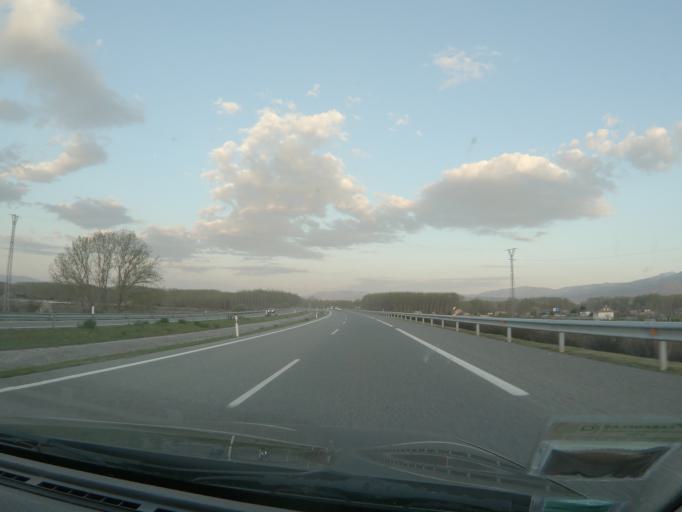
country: ES
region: Castille and Leon
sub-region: Provincia de Leon
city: Villadecanes
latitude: 42.5708
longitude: -6.7514
